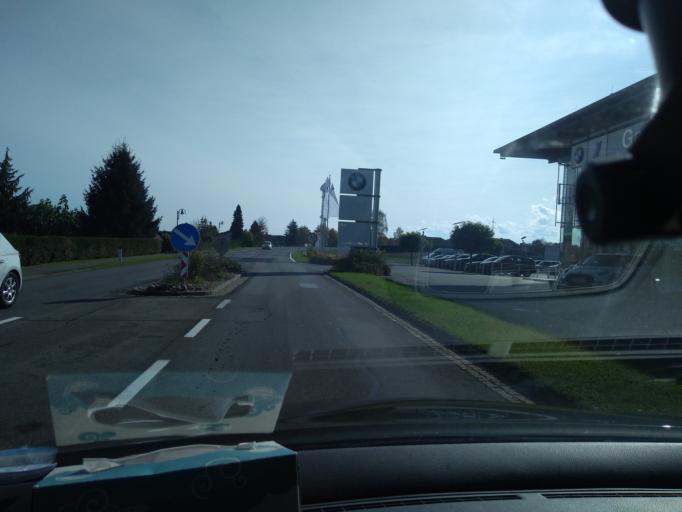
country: AT
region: Styria
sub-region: Politischer Bezirk Leibnitz
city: Lang
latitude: 46.8465
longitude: 15.5382
